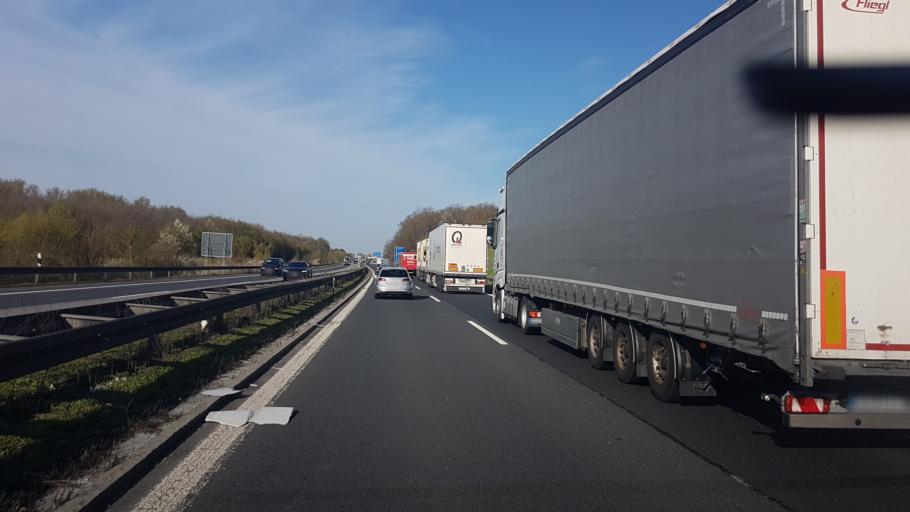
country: DE
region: Bavaria
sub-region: Regierungsbezirk Unterfranken
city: Sennfeld
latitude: 50.0284
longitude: 10.2535
